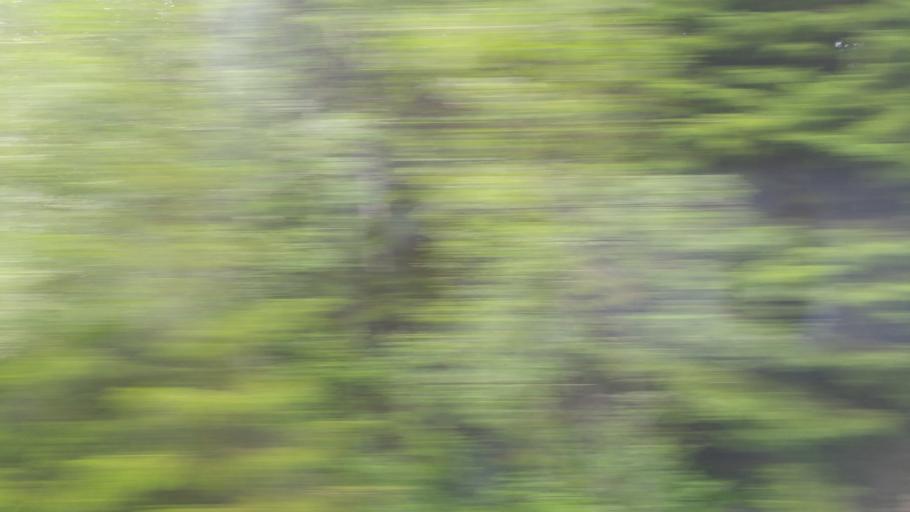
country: SE
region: Jaemtland
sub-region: Are Kommun
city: Are
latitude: 63.3868
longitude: 12.8983
